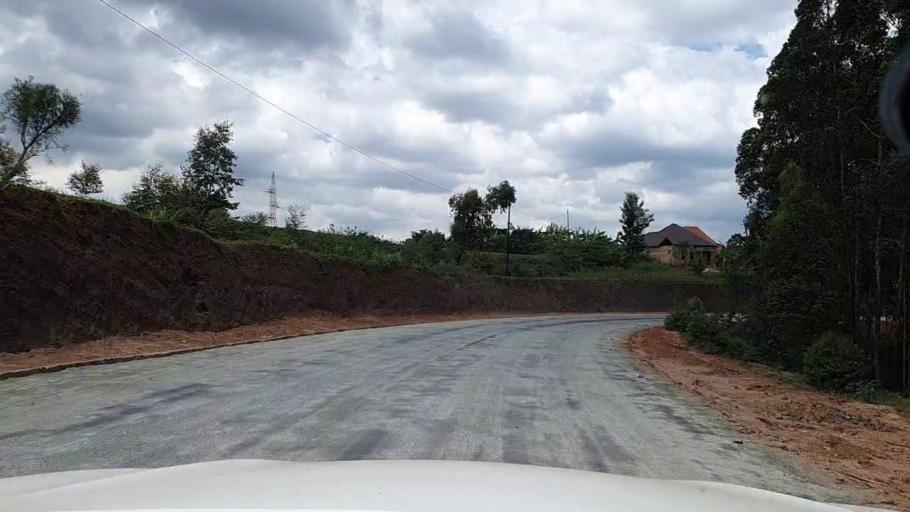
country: RW
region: Southern Province
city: Butare
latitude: -2.6988
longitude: 29.5692
